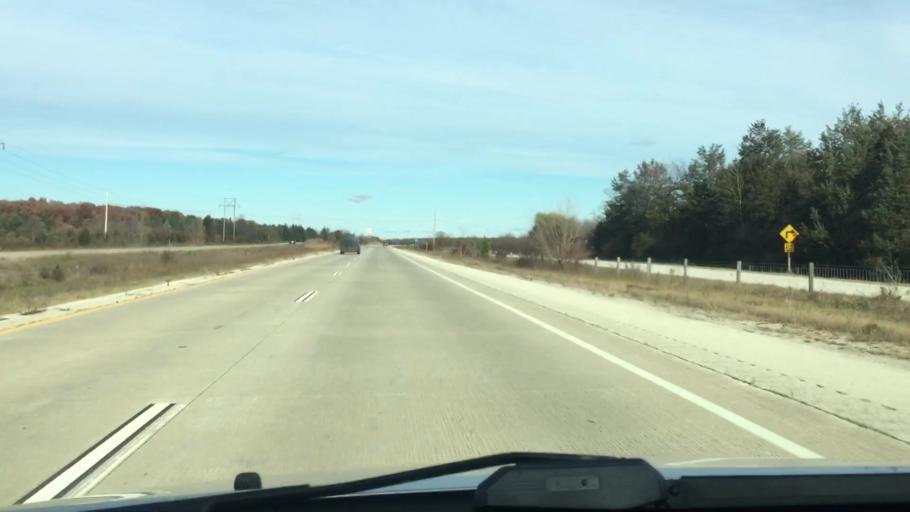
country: US
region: Wisconsin
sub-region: Kewaunee County
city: Luxemburg
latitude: 44.6133
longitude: -87.8342
